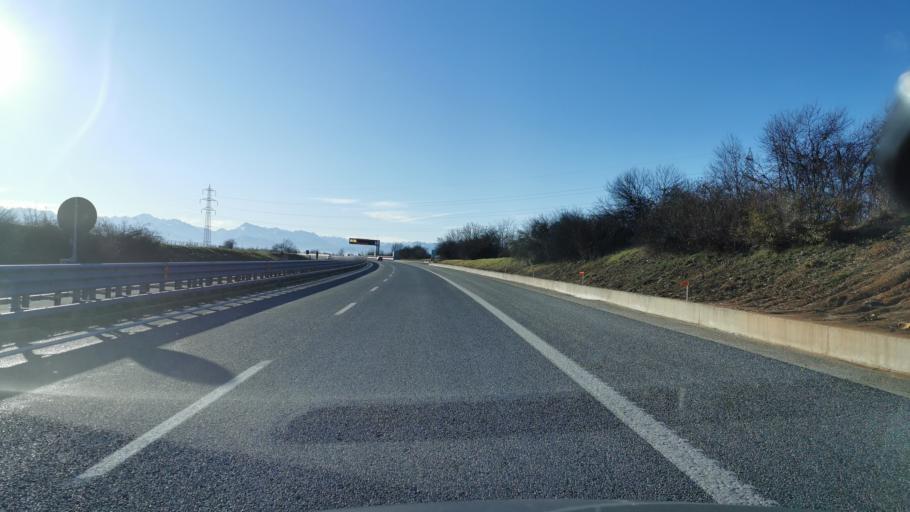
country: IT
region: Piedmont
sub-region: Provincia di Cuneo
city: Magliano Alpi
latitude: 44.4841
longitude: 7.8034
